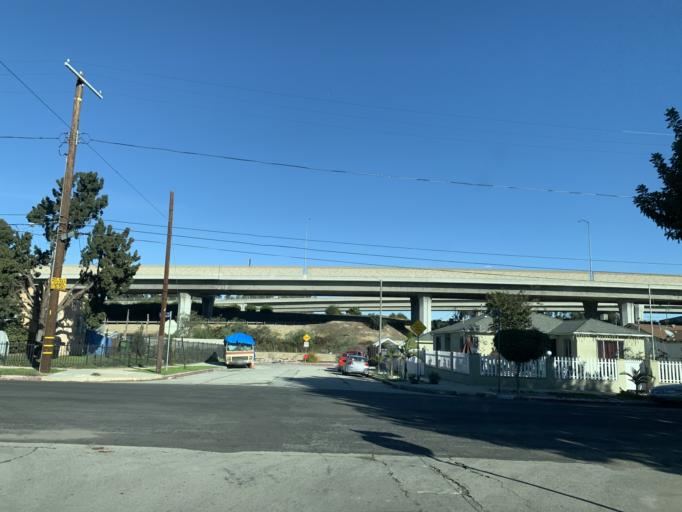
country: US
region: California
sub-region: Los Angeles County
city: West Athens
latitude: 33.9272
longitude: -118.2848
